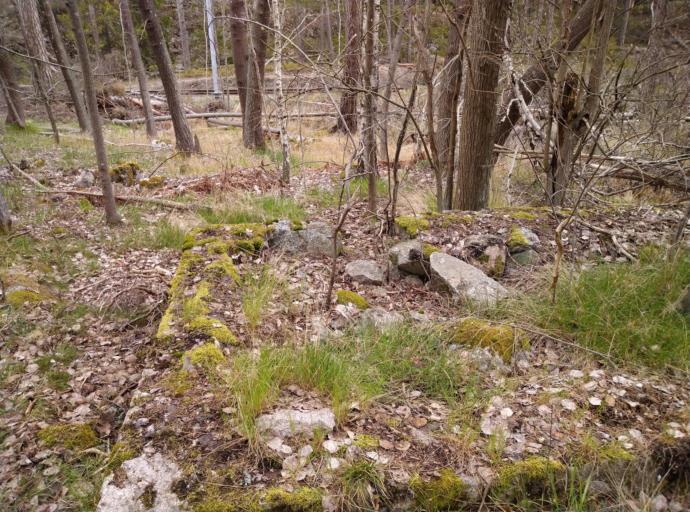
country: SE
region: Stockholm
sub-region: Nacka Kommun
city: Fisksatra
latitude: 59.2941
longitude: 18.2666
